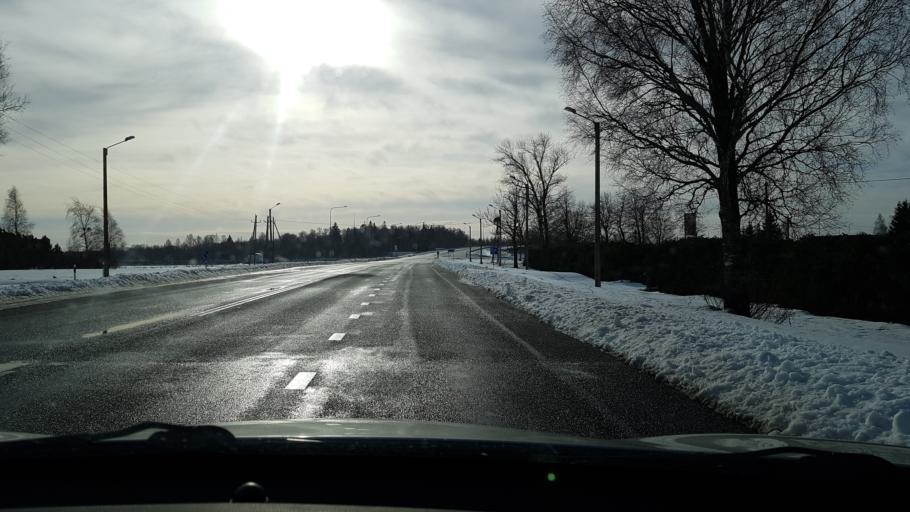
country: EE
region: Jaervamaa
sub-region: Paide linn
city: Paide
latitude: 58.9201
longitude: 25.6128
